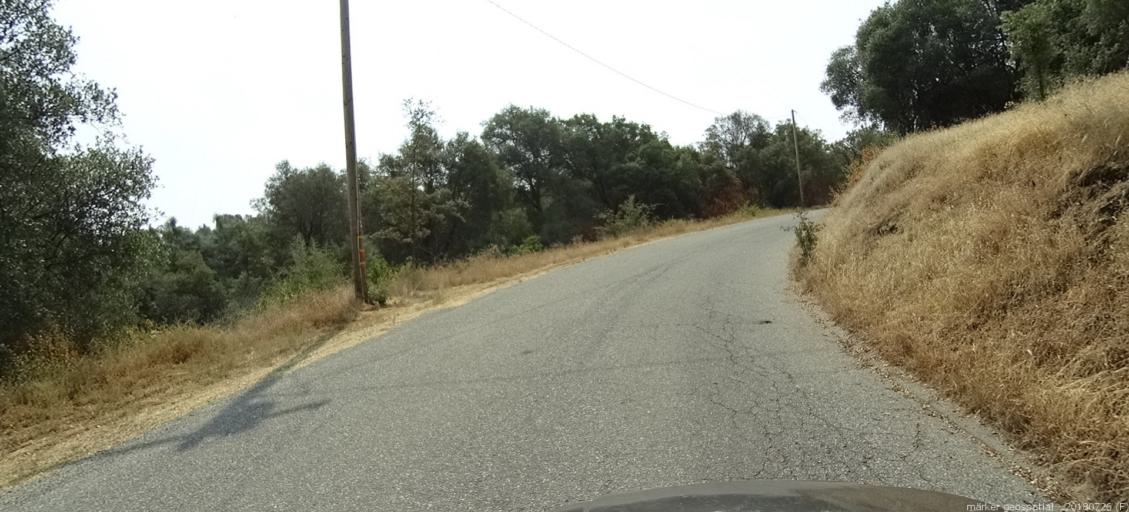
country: US
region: California
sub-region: Madera County
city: Coarsegold
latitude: 37.2375
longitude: -119.6947
